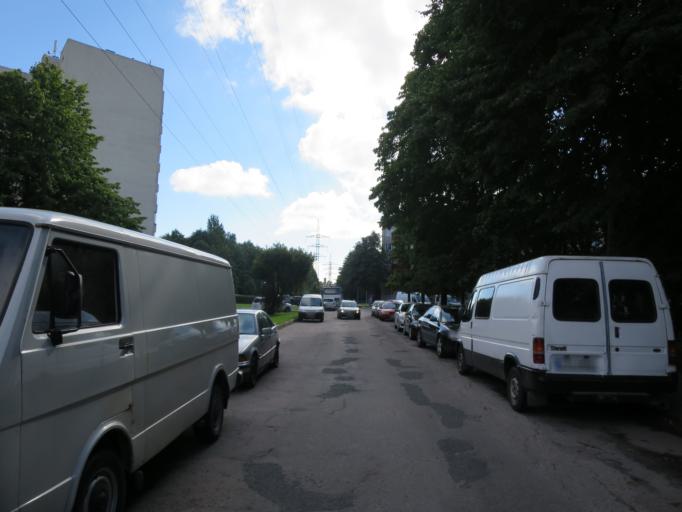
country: EE
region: Harju
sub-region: Tallinna linn
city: Tallinn
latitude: 59.4045
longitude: 24.7085
